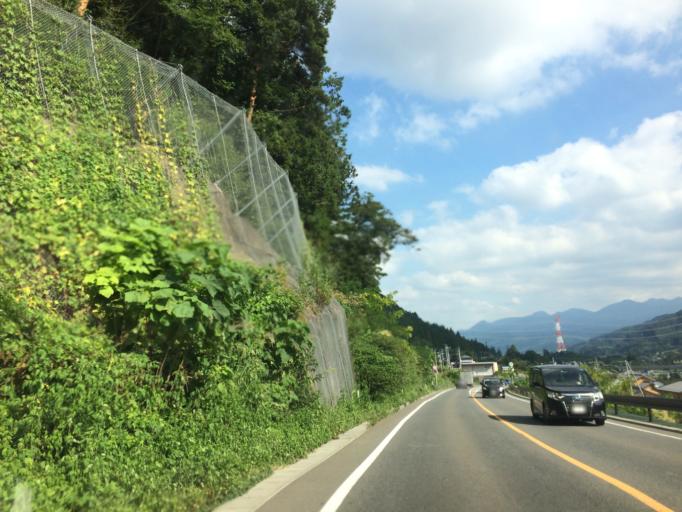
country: JP
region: Gunma
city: Nakanojomachi
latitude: 36.5727
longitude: 138.7412
